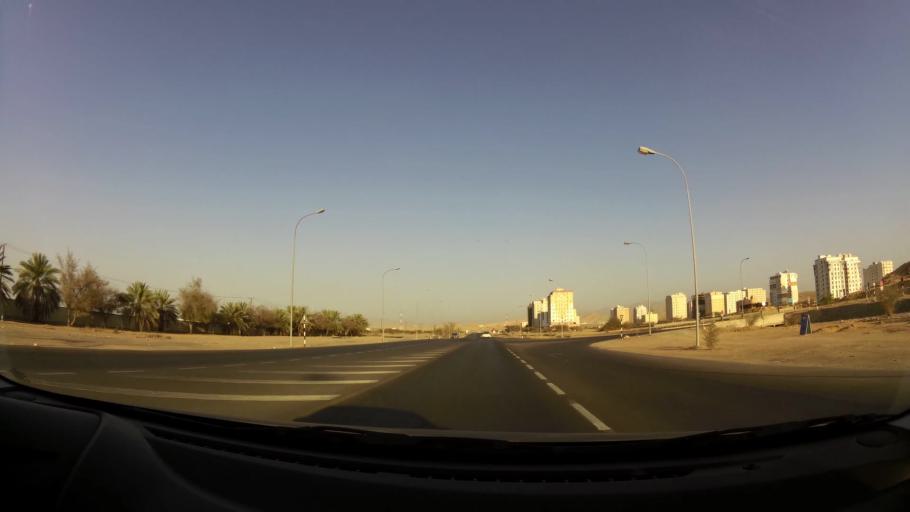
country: OM
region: Muhafazat Masqat
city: As Sib al Jadidah
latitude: 23.5790
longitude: 58.1774
